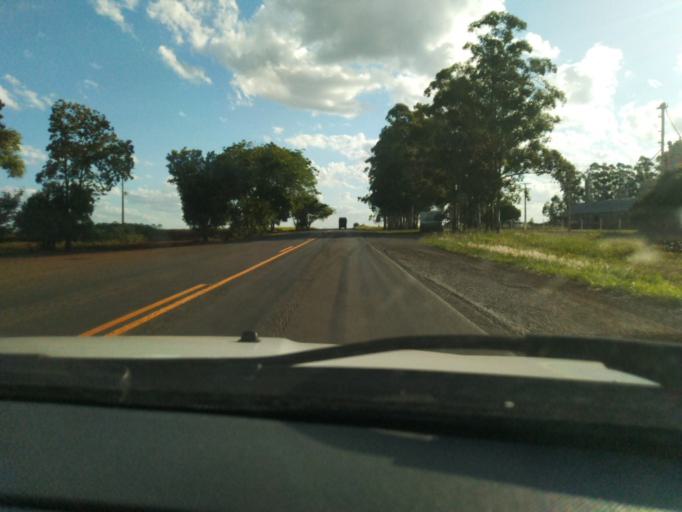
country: AR
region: Corrientes
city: Garruchos
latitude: -28.5512
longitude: -55.5674
